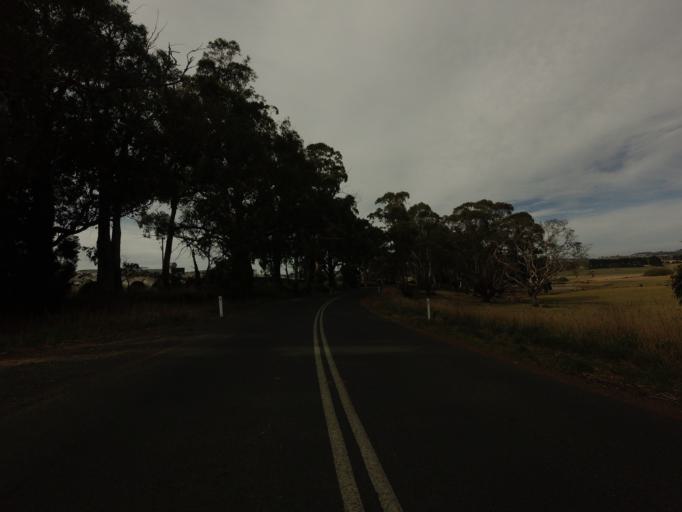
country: AU
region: Tasmania
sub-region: Sorell
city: Sorell
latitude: -42.4256
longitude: 147.4676
